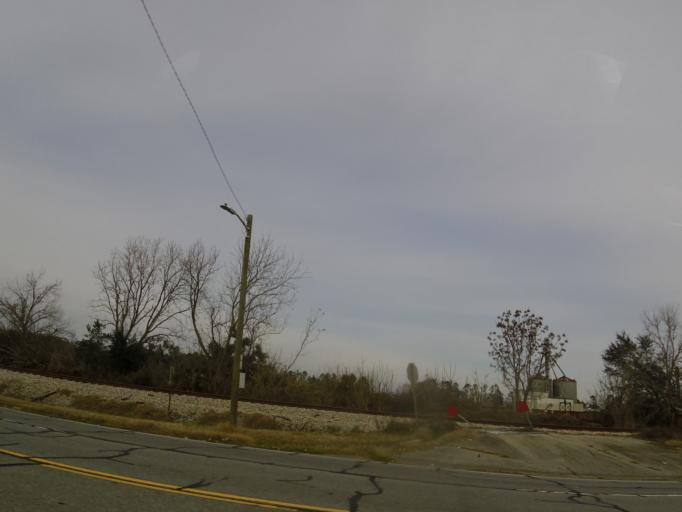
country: US
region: Georgia
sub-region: Seminole County
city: Donalsonville
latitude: 31.0367
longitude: -84.8671
